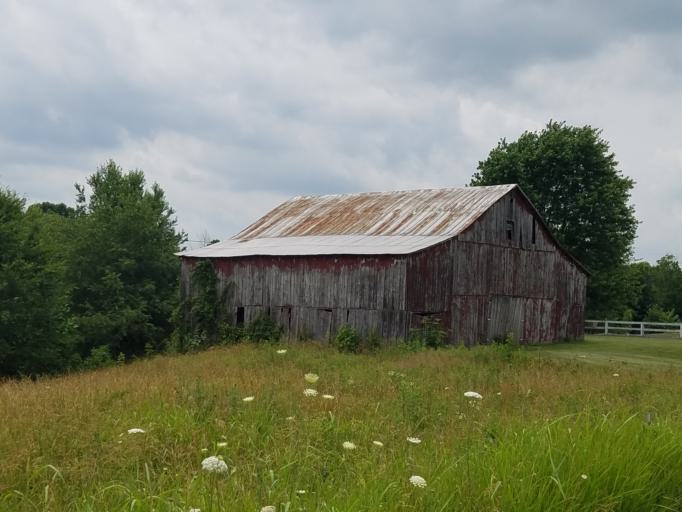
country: US
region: Kentucky
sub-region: Grayson County
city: Leitchfield
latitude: 37.3739
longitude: -86.1069
